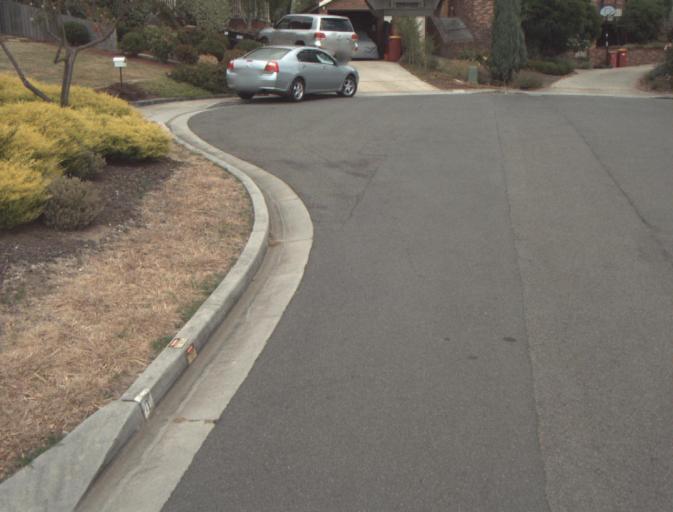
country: AU
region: Tasmania
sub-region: Launceston
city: Summerhill
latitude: -41.4678
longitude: 147.1474
